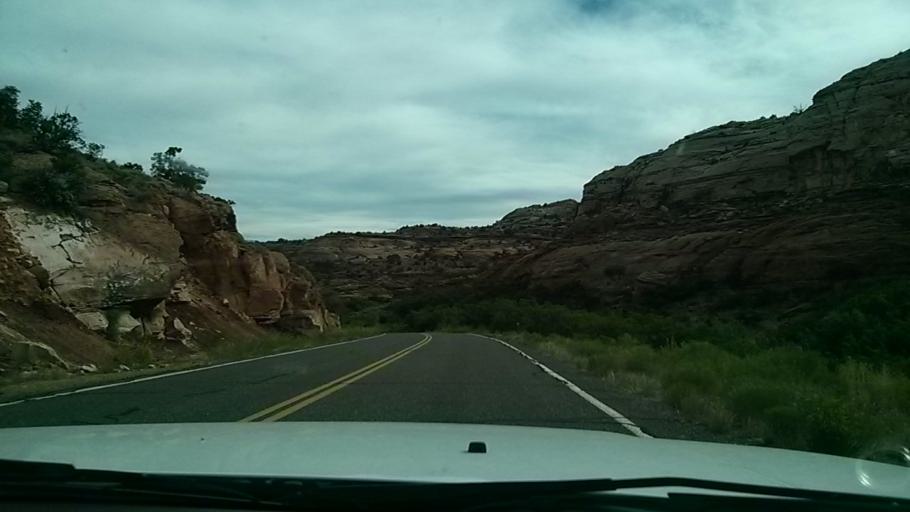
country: US
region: Utah
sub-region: Wayne County
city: Loa
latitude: 37.7875
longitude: -111.4164
